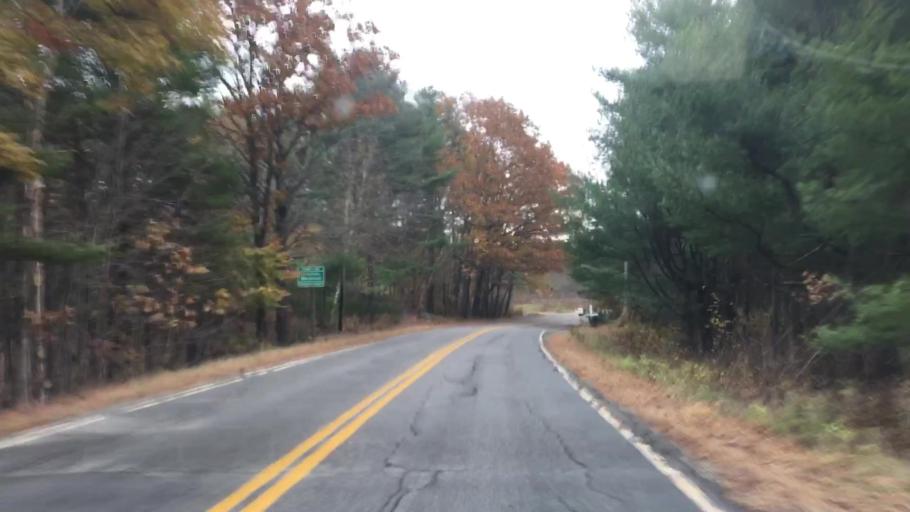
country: US
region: Maine
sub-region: Lincoln County
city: Whitefield
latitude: 44.1703
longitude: -69.6613
